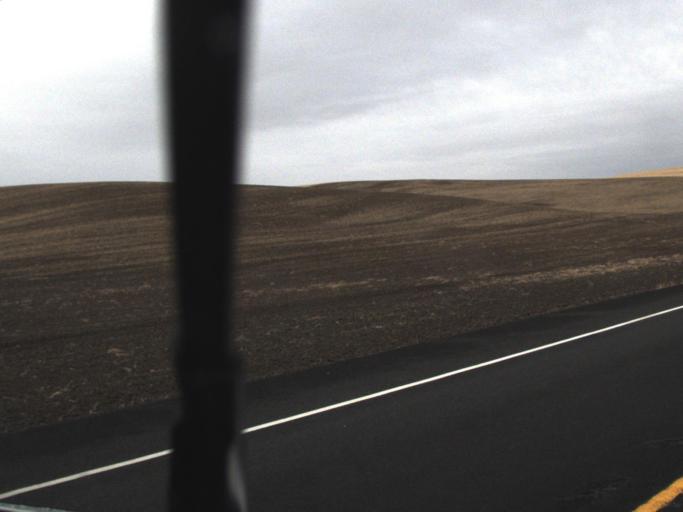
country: US
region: Washington
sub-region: Whitman County
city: Pullman
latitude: 46.6860
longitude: -117.2005
